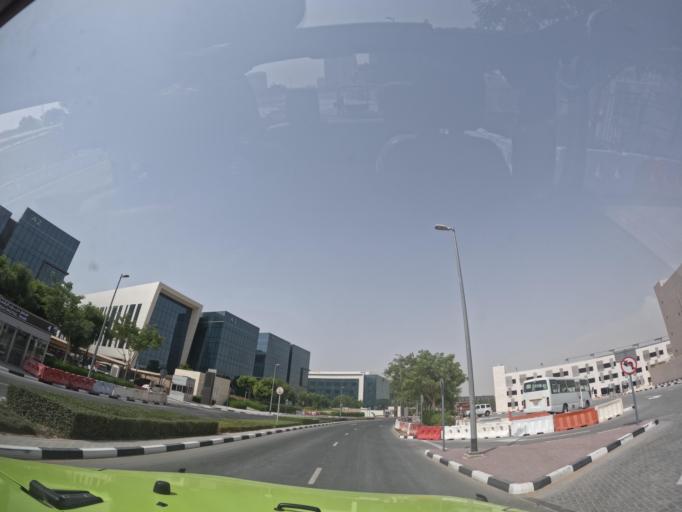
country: AE
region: Dubai
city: Dubai
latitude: 25.1178
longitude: 55.3781
